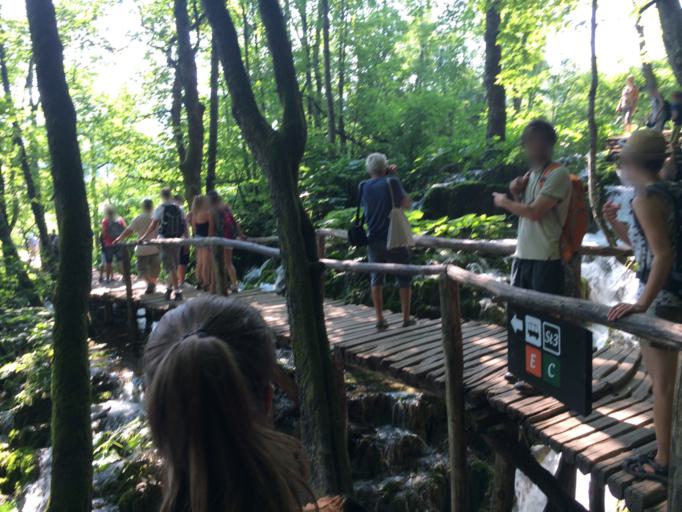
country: HR
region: Licko-Senjska
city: Jezerce
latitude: 44.8742
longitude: 15.6011
